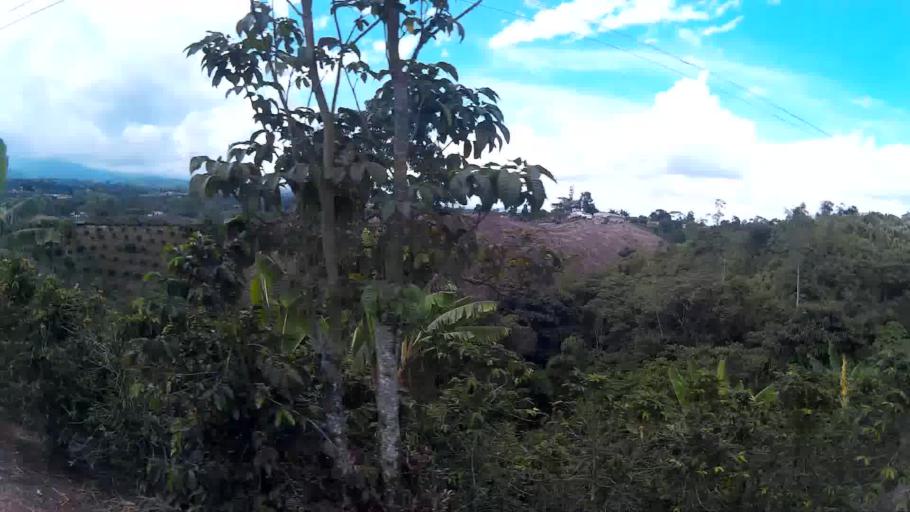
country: CO
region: Valle del Cauca
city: Ulloa
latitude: 4.7502
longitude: -75.7142
